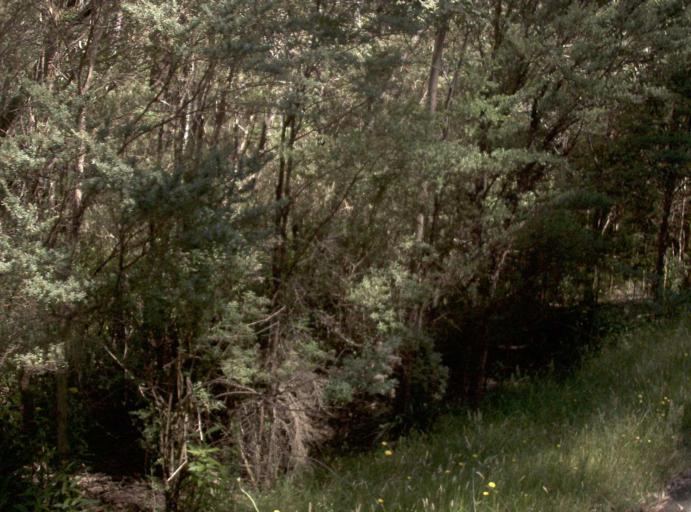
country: AU
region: Victoria
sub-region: Yarra Ranges
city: Millgrove
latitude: -37.7138
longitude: 145.6745
